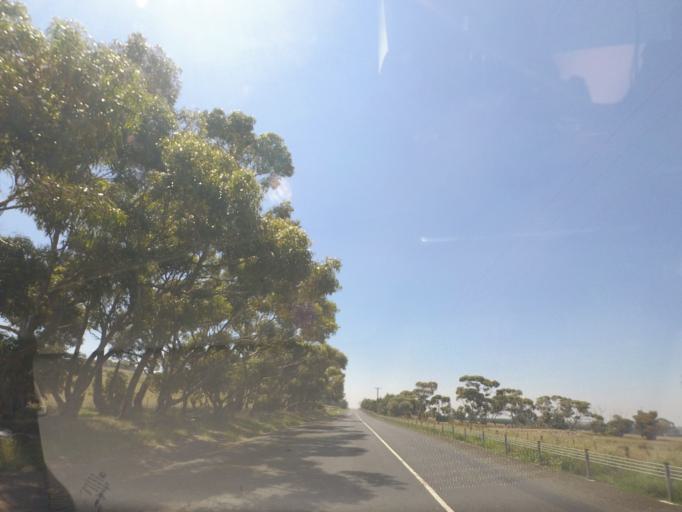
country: AU
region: Victoria
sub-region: Hume
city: Greenvale
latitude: -37.5879
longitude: 144.8640
